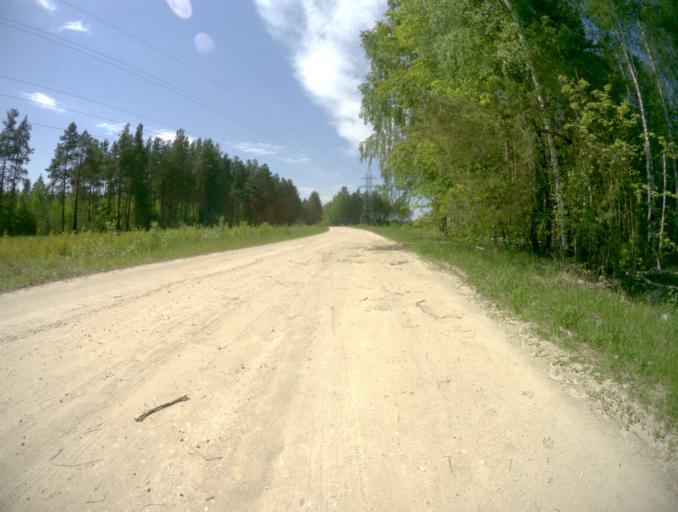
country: RU
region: Vladimir
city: Gusevskiy
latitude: 55.6866
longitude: 40.5110
